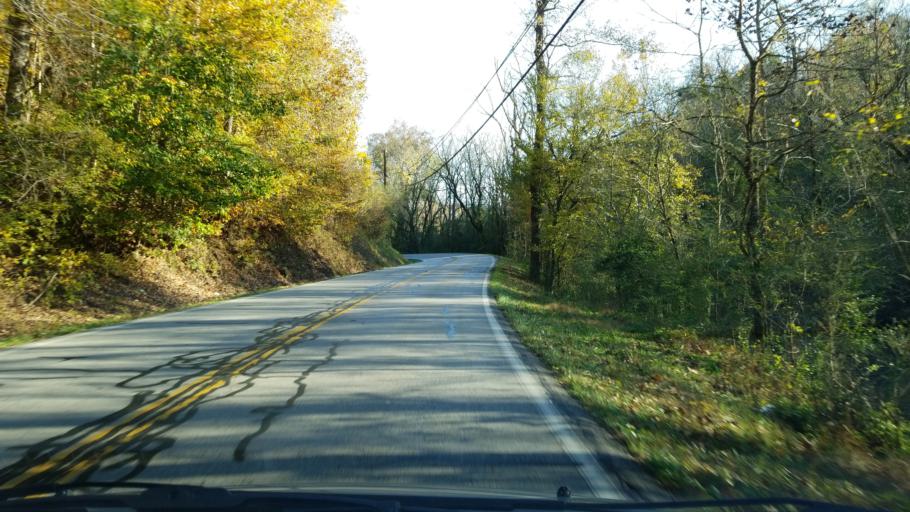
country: US
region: Tennessee
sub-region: Hamilton County
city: Falling Water
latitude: 35.1963
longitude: -85.2455
